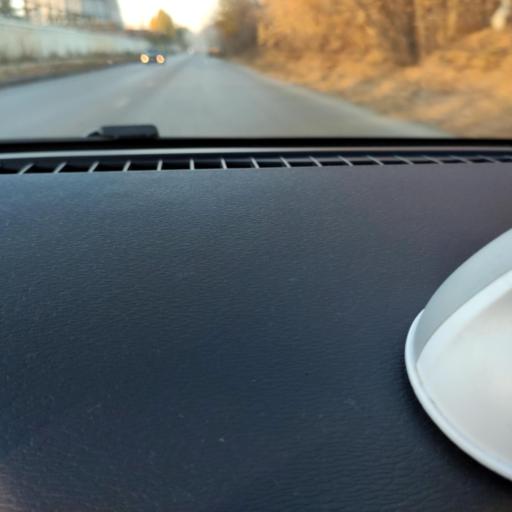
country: RU
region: Samara
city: Petra-Dubrava
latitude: 53.2533
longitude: 50.2752
